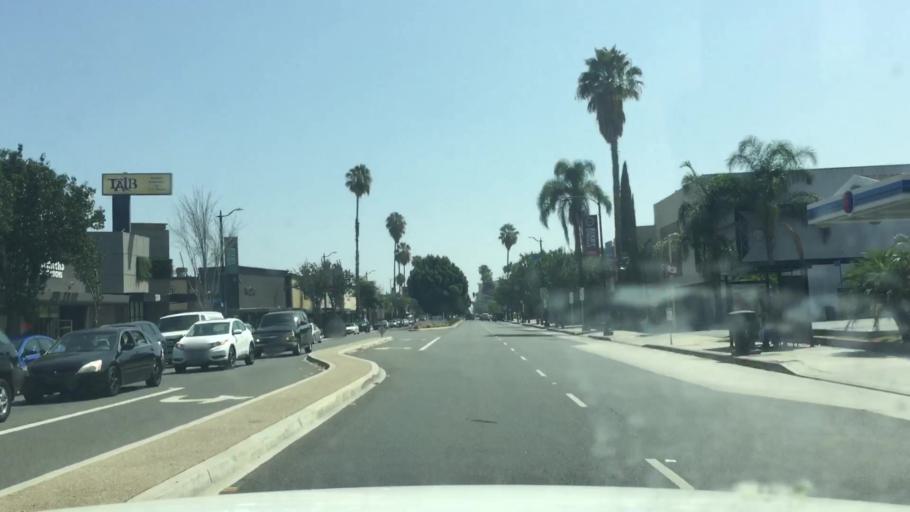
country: US
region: California
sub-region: Los Angeles County
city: Signal Hill
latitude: 33.8365
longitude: -118.1851
